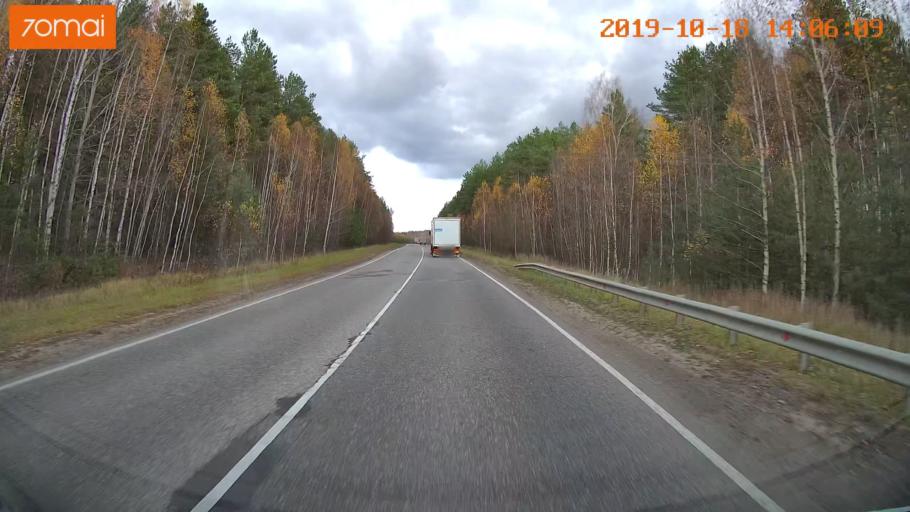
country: RU
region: Rjazan
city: Spas-Klepiki
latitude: 55.1419
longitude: 40.1490
